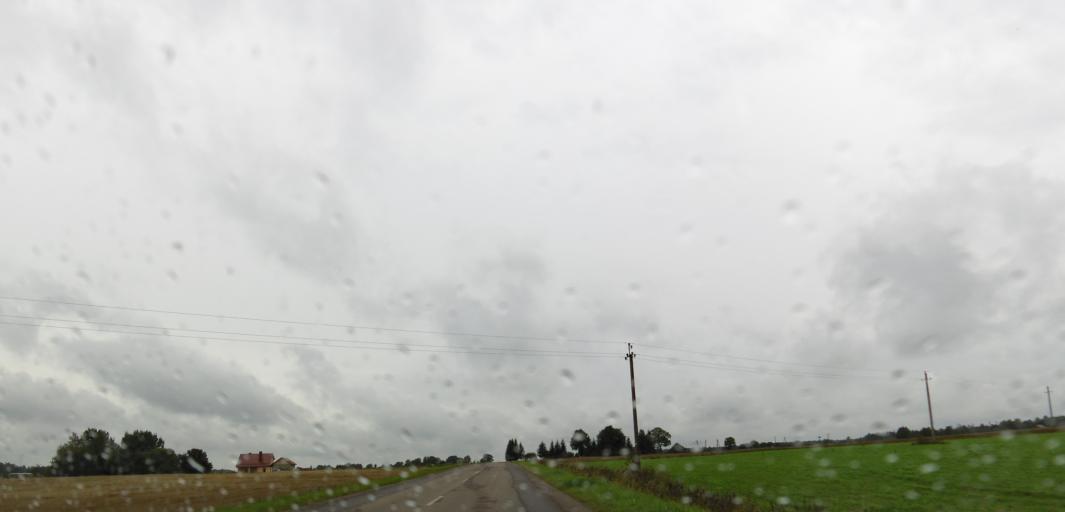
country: LT
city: Sirvintos
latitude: 55.0880
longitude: 24.9888
